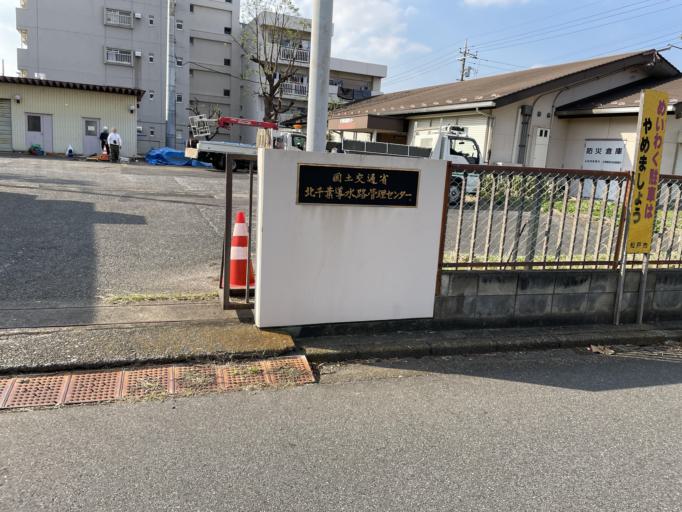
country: JP
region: Chiba
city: Nagareyama
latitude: 35.8297
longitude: 139.9070
